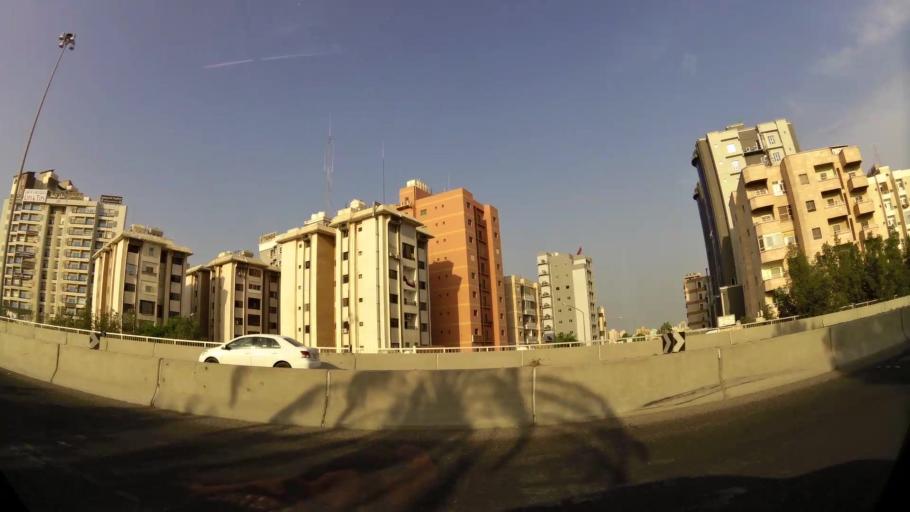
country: KW
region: Muhafazat Hawalli
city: Hawalli
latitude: 29.3183
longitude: 48.0167
